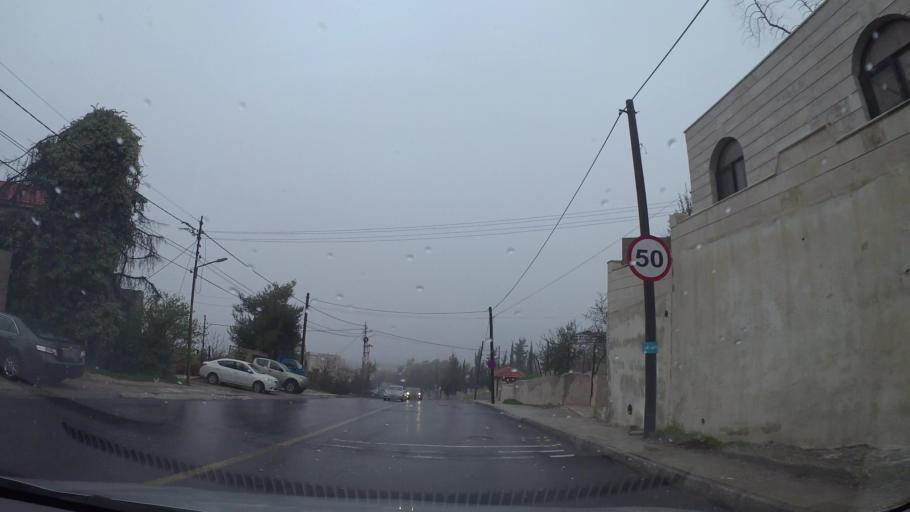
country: JO
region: Amman
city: Al Jubayhah
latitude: 32.0256
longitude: 35.8330
